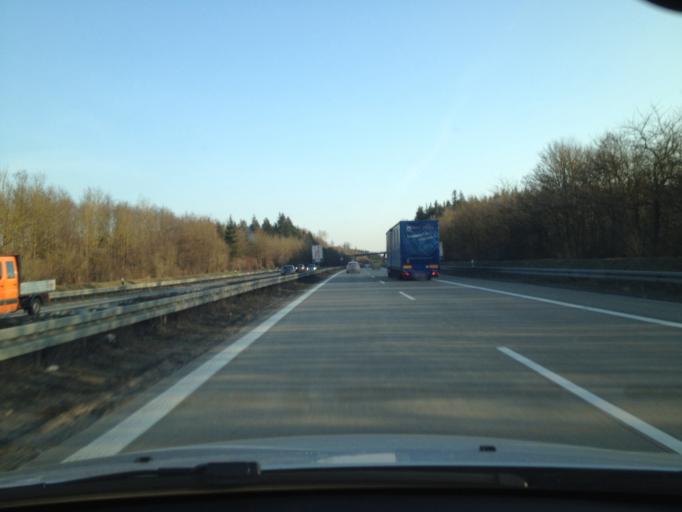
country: DE
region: Baden-Wuerttemberg
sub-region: Regierungsbezirk Stuttgart
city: Nattheim
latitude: 48.7128
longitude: 10.2110
